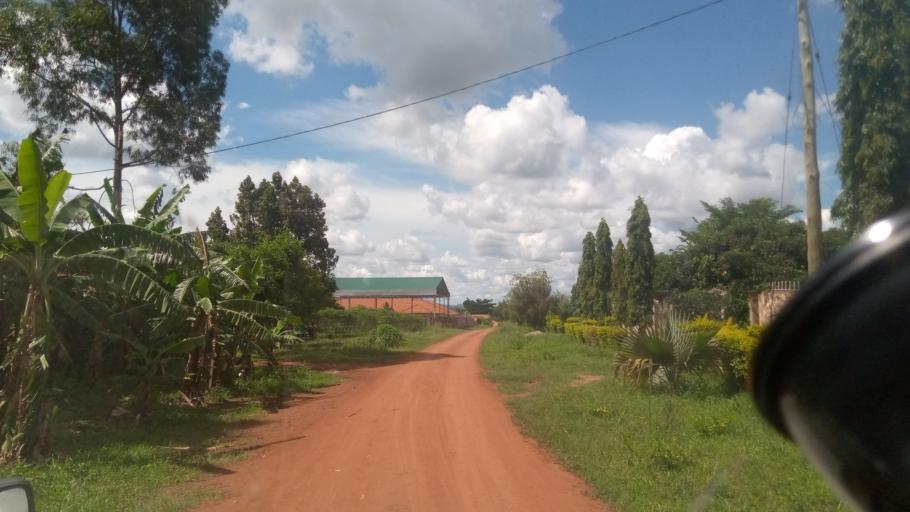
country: UG
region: Northern Region
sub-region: Lira District
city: Lira
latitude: 2.2363
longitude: 32.9047
